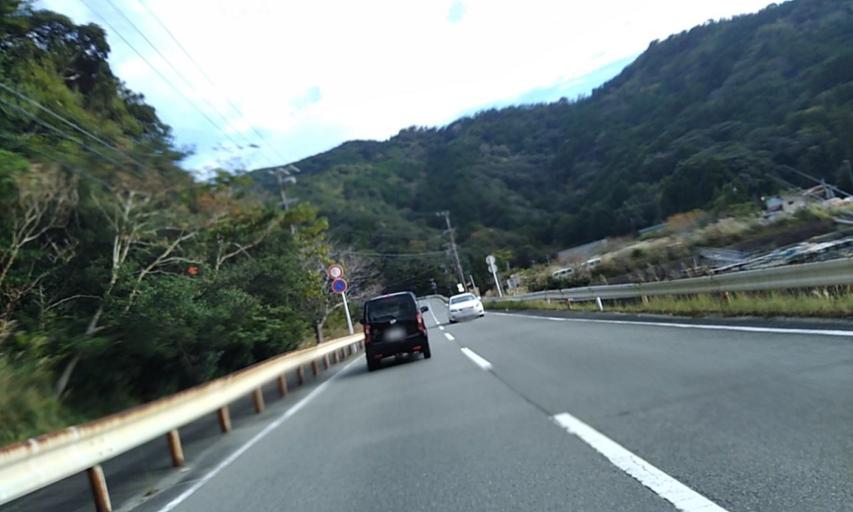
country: JP
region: Mie
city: Ise
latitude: 34.2571
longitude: 136.4691
